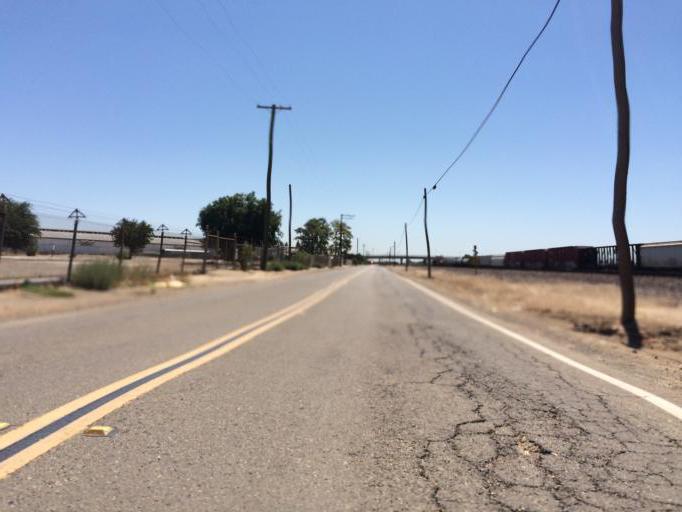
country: US
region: California
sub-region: Fresno County
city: Fresno
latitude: 36.7116
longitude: -119.7701
